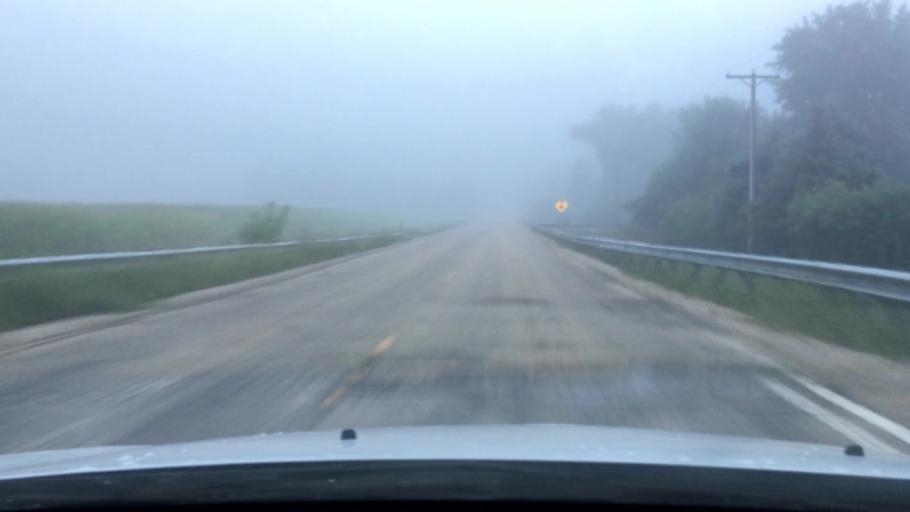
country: US
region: Illinois
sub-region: DeKalb County
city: Waterman
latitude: 41.7781
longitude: -88.7739
